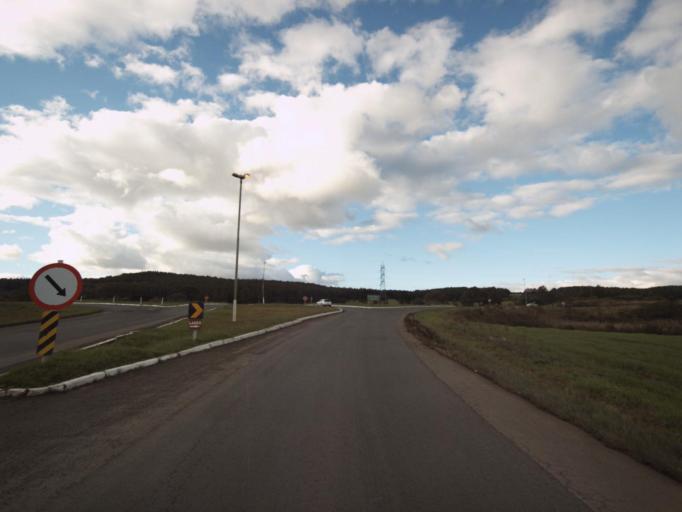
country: BR
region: Santa Catarina
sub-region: Campos Novos
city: Campos Novos
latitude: -27.3944
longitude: -51.1926
